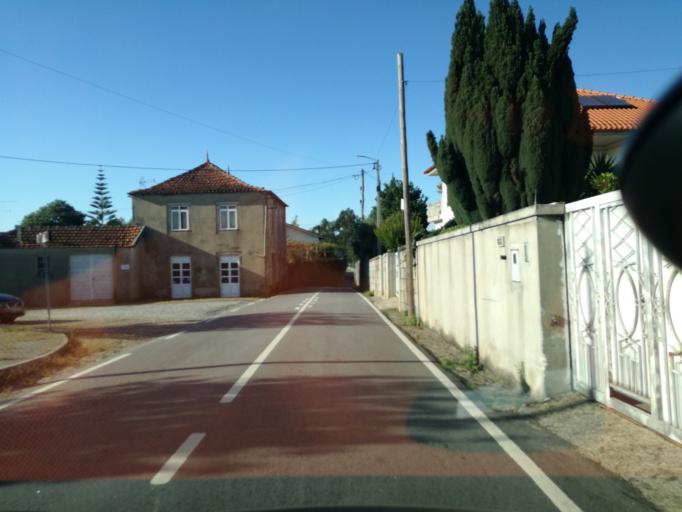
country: PT
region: Porto
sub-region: Santo Tirso
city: Sao Miguel do Couto
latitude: 41.3080
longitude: -8.4615
